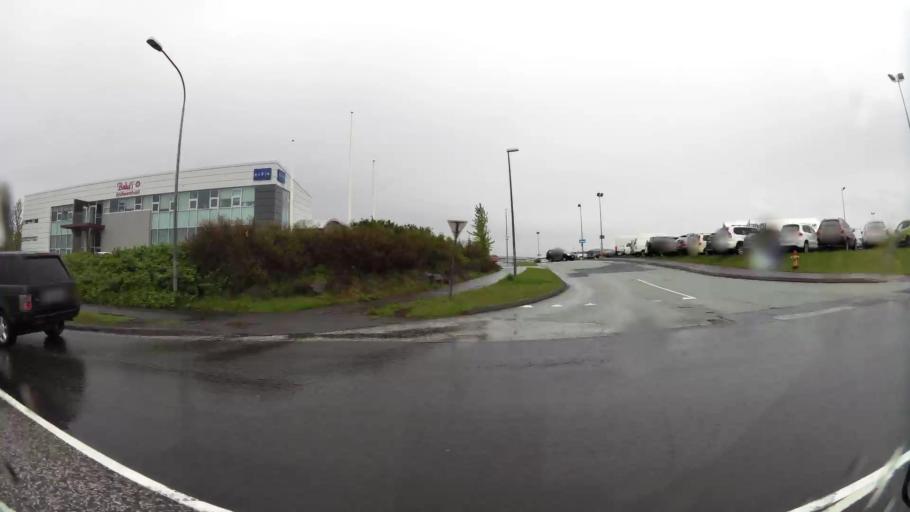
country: IS
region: Capital Region
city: Mosfellsbaer
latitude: 64.1164
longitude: -21.7854
